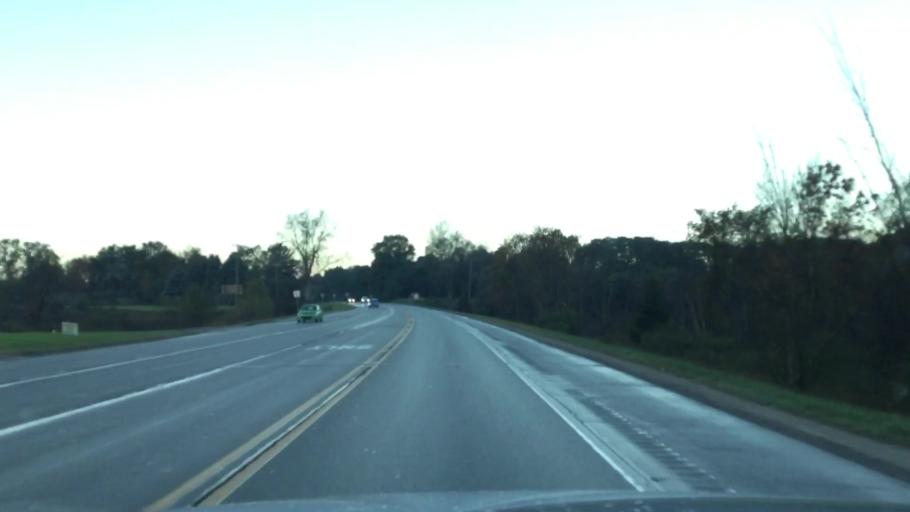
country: US
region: Michigan
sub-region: Livingston County
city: Howell
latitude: 42.6294
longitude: -83.8764
